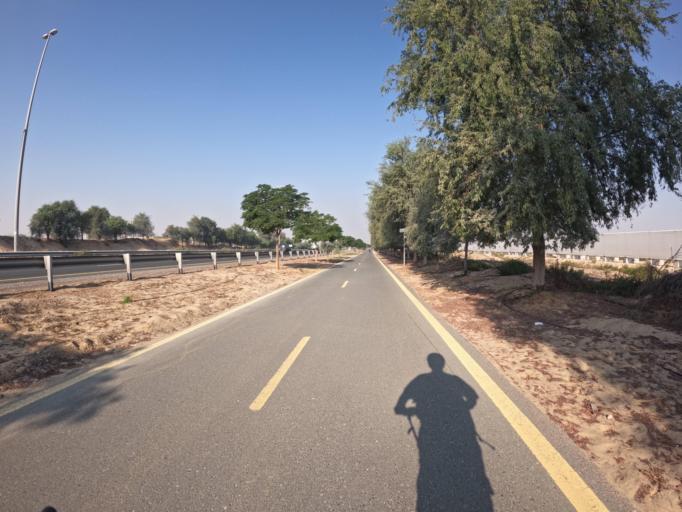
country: AE
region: Dubai
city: Dubai
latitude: 24.9930
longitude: 55.3154
